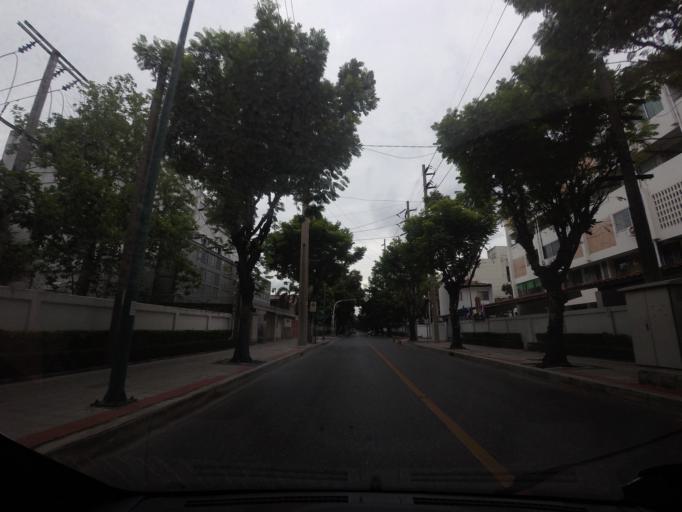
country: TH
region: Bangkok
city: Ratchathewi
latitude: 13.7637
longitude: 100.5325
